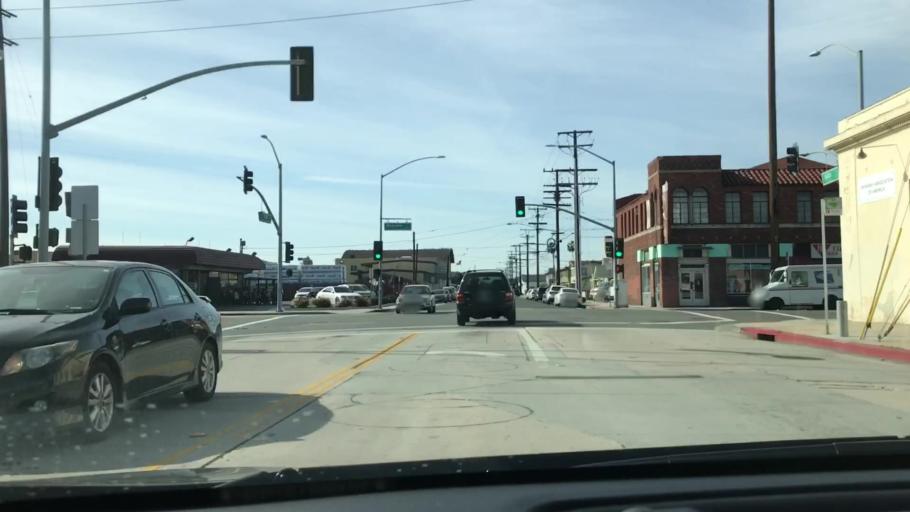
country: US
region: California
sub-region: Los Angeles County
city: Gardena
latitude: 33.8801
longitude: -118.3088
